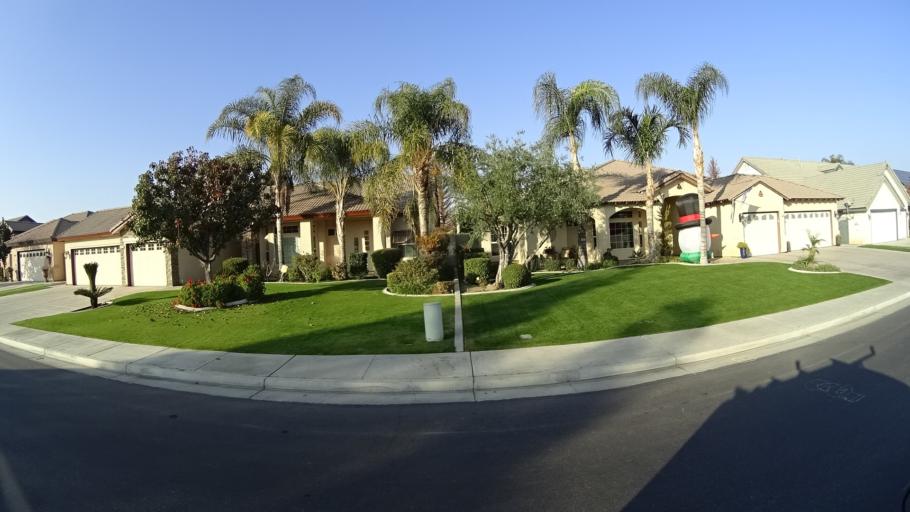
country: US
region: California
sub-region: Kern County
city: Rosedale
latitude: 35.3816
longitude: -119.1509
